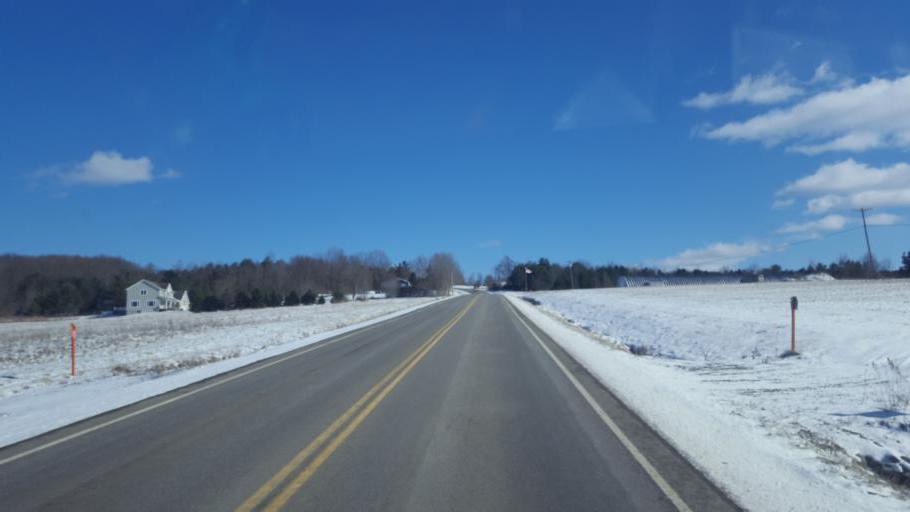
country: US
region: New York
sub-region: Allegany County
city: Friendship
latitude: 42.2040
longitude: -78.1176
